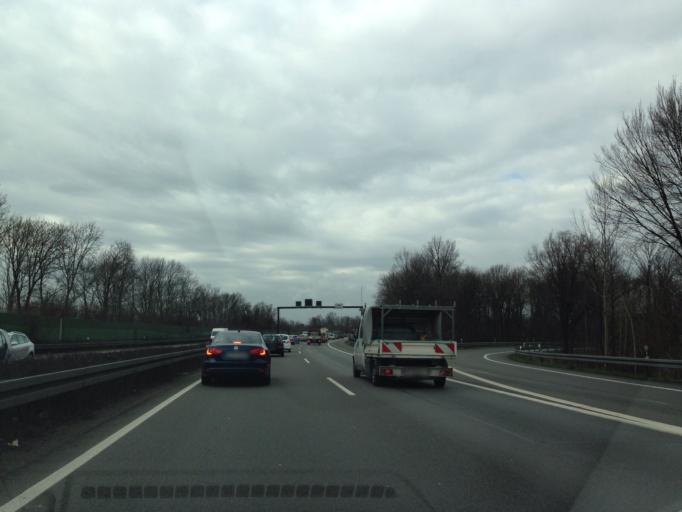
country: DE
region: North Rhine-Westphalia
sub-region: Regierungsbezirk Arnsberg
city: Herne
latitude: 51.5146
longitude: 7.2153
